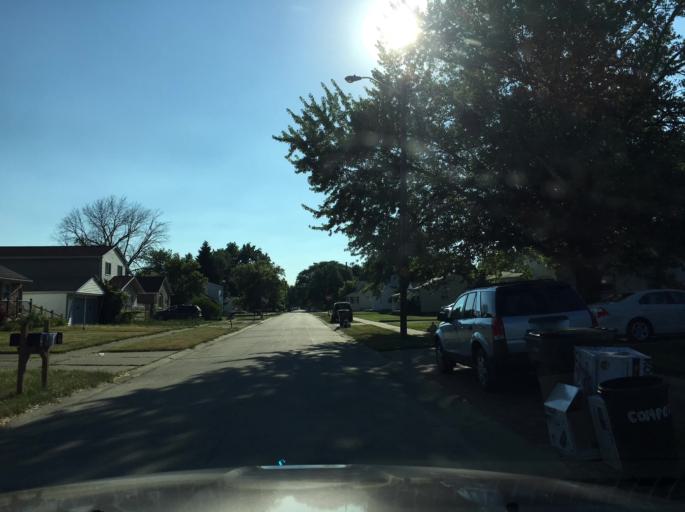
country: US
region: Michigan
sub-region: Macomb County
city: Fraser
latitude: 42.5435
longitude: -82.9155
